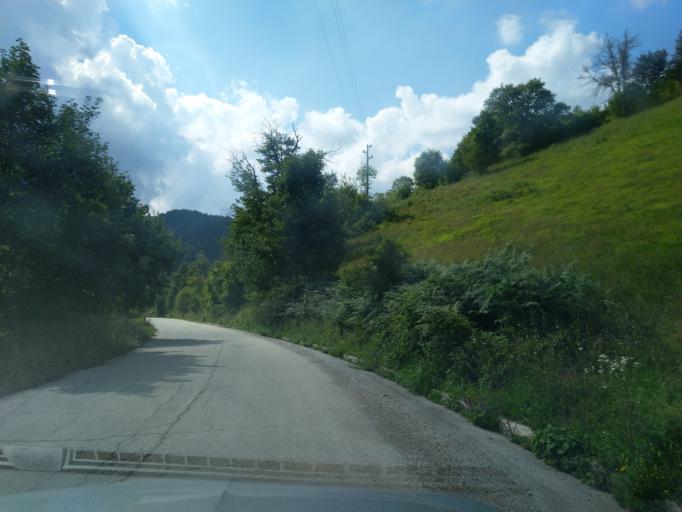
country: RS
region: Central Serbia
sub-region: Zlatiborski Okrug
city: Nova Varos
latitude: 43.5883
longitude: 19.8673
